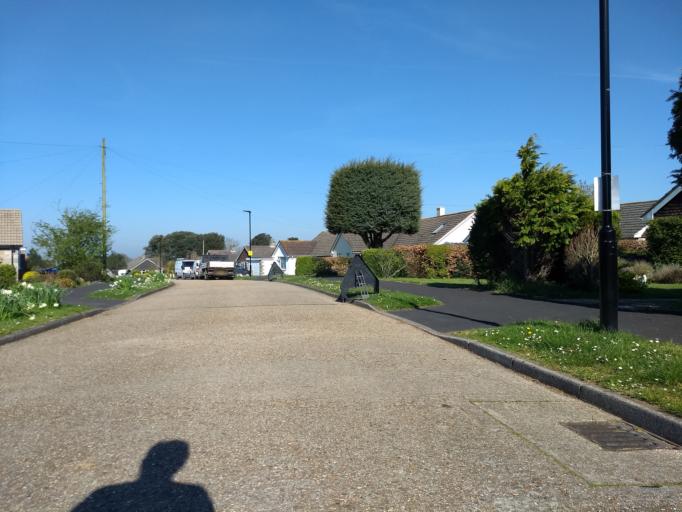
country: GB
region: England
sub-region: Isle of Wight
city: East Cowes
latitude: 50.7283
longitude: -1.2413
